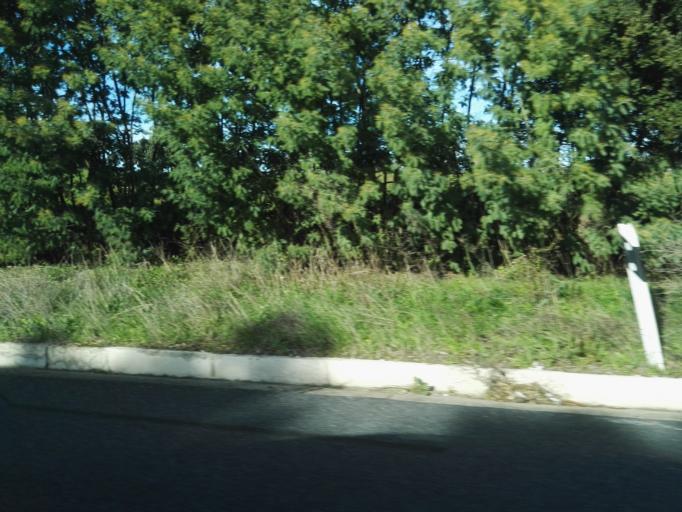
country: PT
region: Evora
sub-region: Estremoz
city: Estremoz
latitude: 38.8368
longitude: -7.6737
